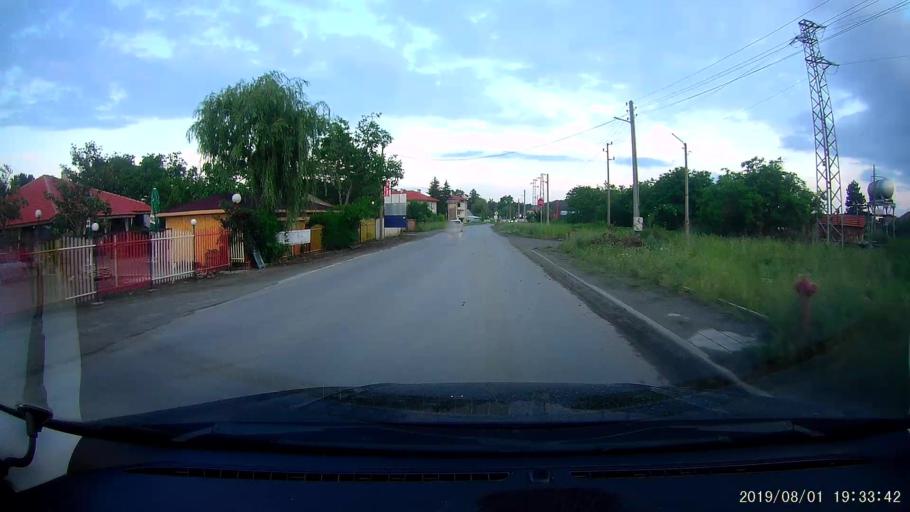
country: BG
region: Burgas
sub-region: Obshtina Sungurlare
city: Sungurlare
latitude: 42.7763
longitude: 26.8773
